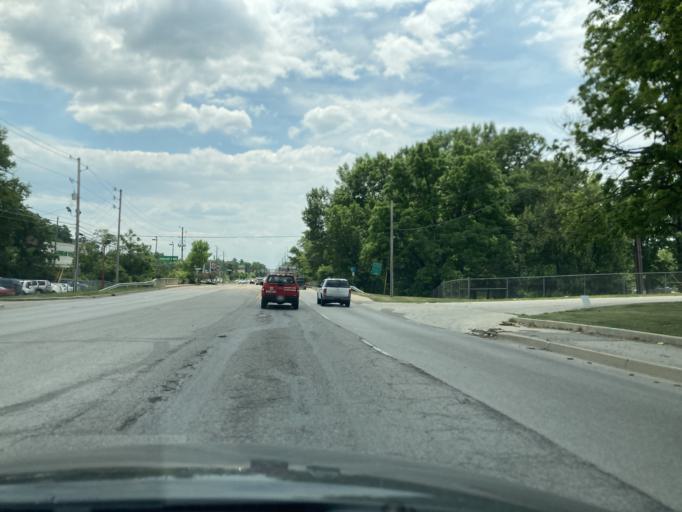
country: US
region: Indiana
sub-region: Marion County
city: Meridian Hills
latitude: 39.8575
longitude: -86.1967
